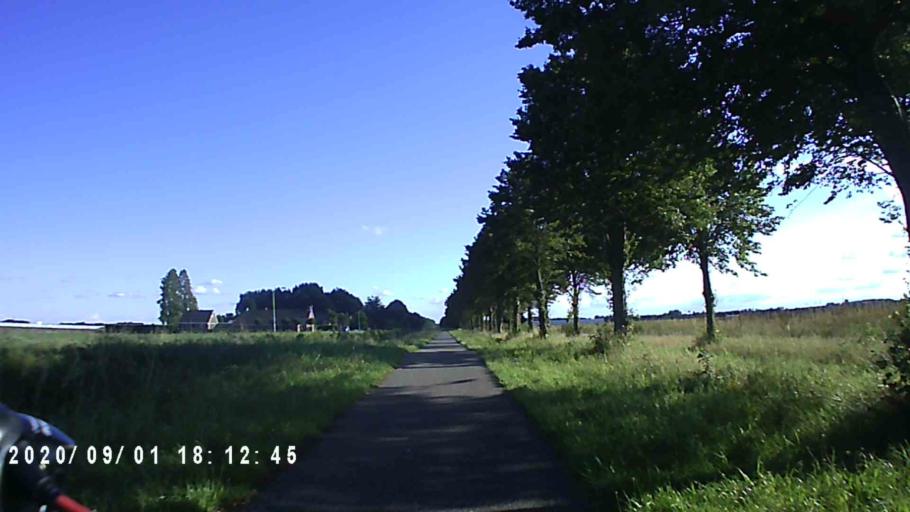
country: NL
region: Groningen
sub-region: Gemeente Hoogezand-Sappemeer
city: Sappemeer
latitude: 53.1859
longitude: 6.7856
